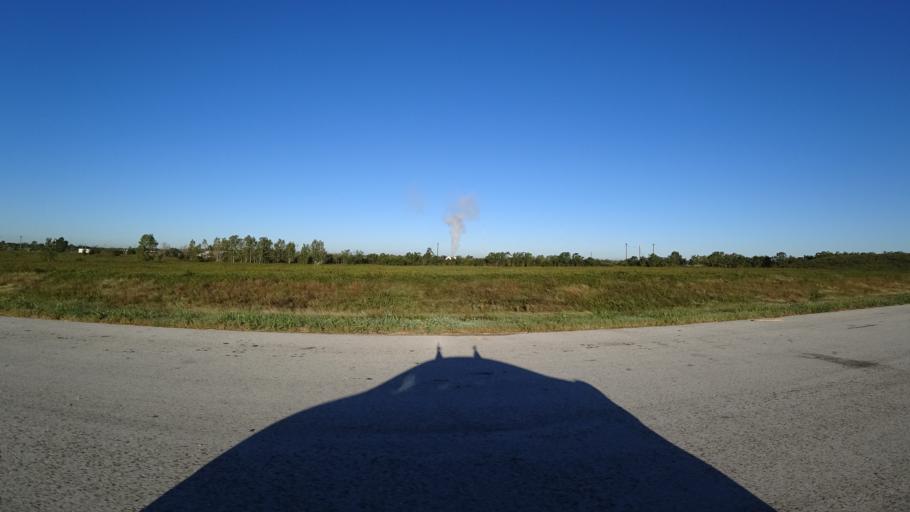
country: US
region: Texas
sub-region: Travis County
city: Hornsby Bend
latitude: 30.2322
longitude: -97.6192
